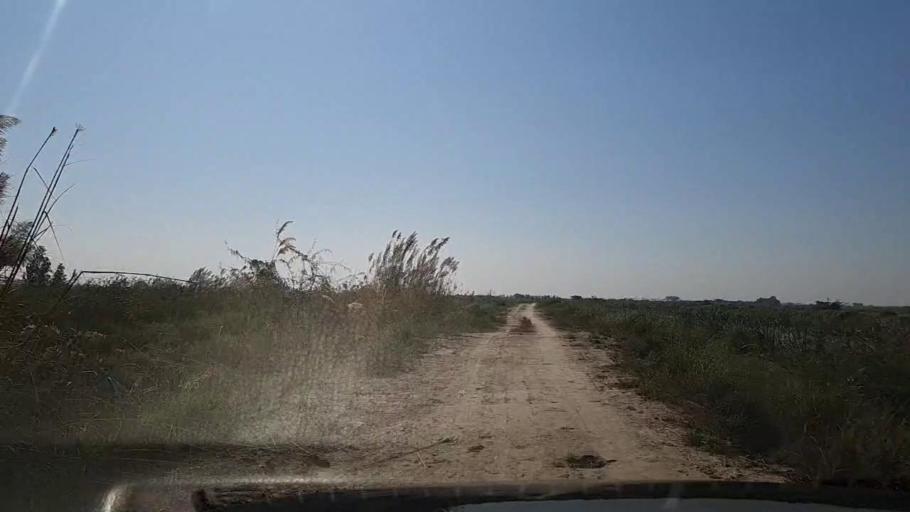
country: PK
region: Sindh
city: Thatta
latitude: 24.6714
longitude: 67.8891
